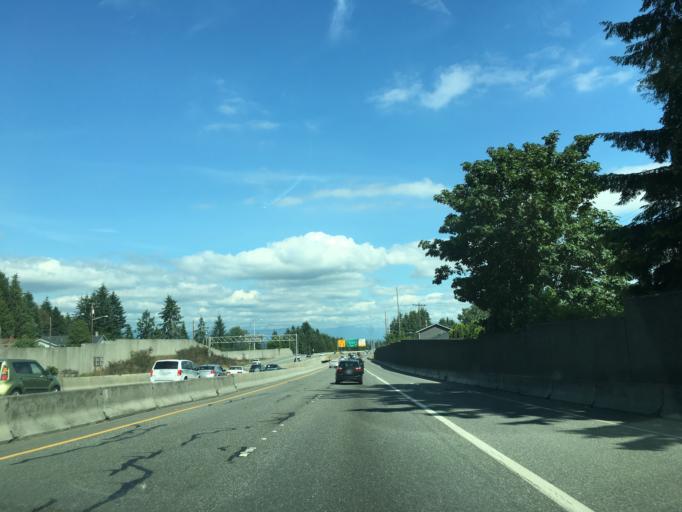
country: US
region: Washington
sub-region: Snohomish County
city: Everett
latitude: 47.9222
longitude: -122.2187
